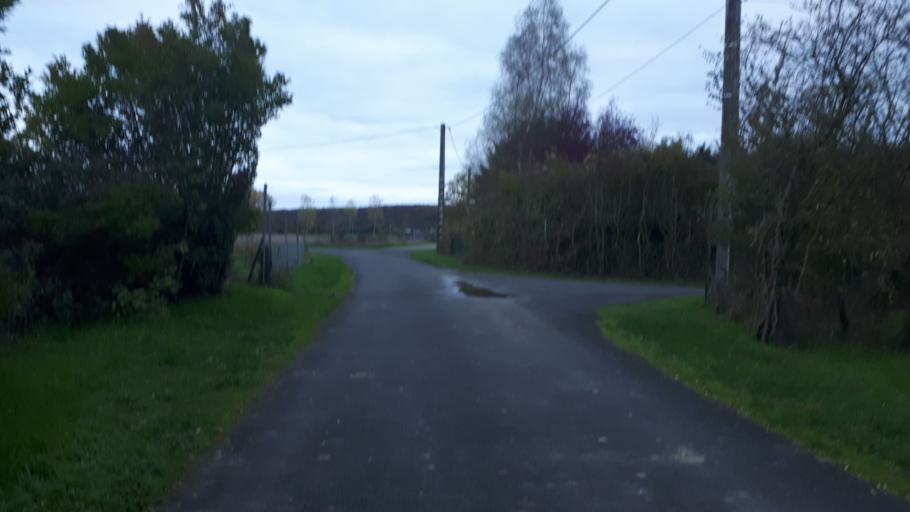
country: FR
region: Centre
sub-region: Departement du Loir-et-Cher
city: Lunay
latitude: 47.7706
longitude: 0.9269
